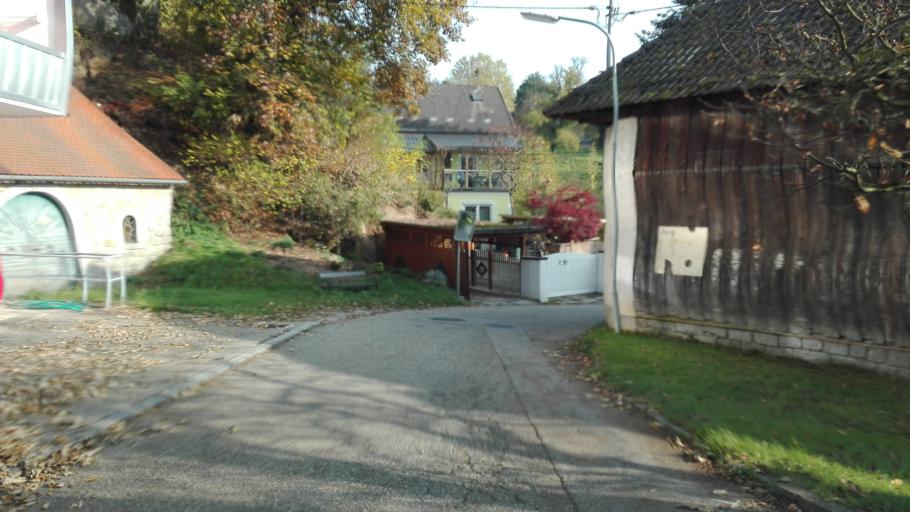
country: AT
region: Upper Austria
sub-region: Politischer Bezirk Perg
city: Perg
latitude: 48.2537
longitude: 14.6316
